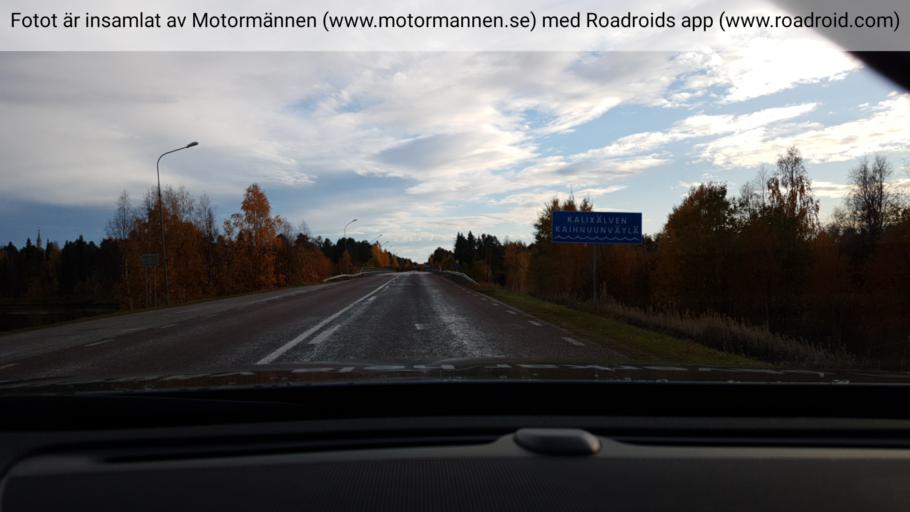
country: SE
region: Norrbotten
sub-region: Pajala Kommun
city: Pajala
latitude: 67.1613
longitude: 22.6326
